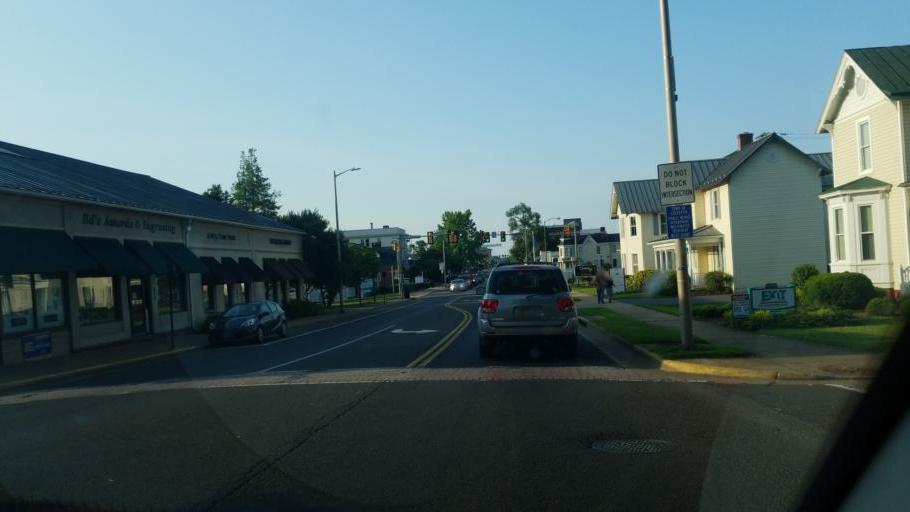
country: US
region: Virginia
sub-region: Culpeper County
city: Culpeper
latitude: 38.4694
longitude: -77.9976
